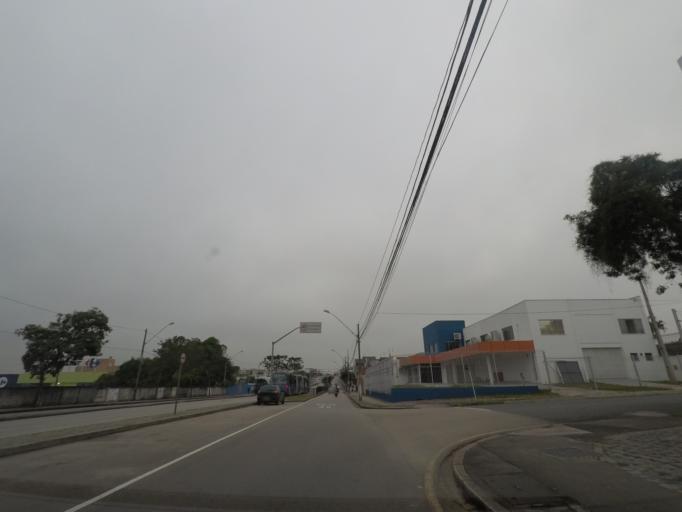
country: BR
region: Parana
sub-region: Curitiba
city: Curitiba
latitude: -25.4538
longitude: -49.2610
